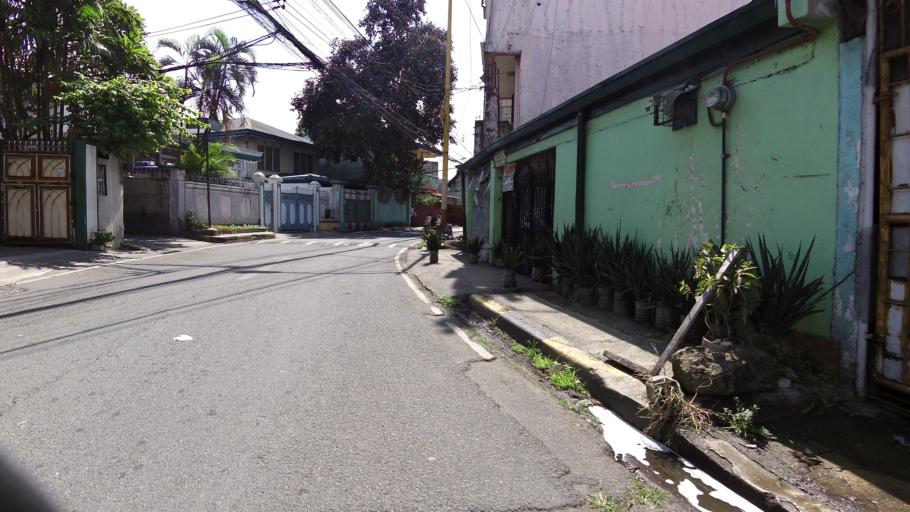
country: PH
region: Calabarzon
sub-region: Province of Rizal
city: Pateros
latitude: 14.5666
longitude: 121.0839
